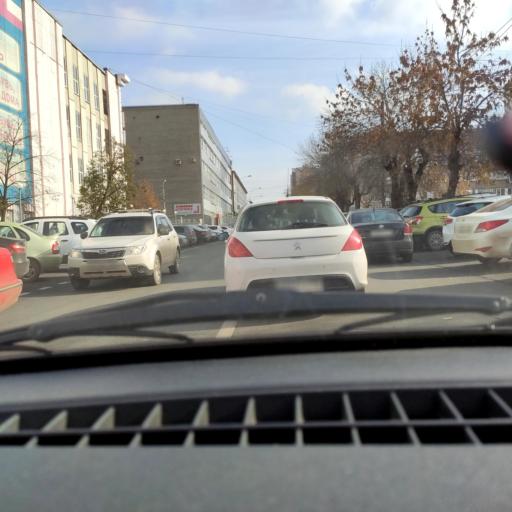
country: RU
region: Bashkortostan
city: Ufa
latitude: 54.7337
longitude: 55.9337
